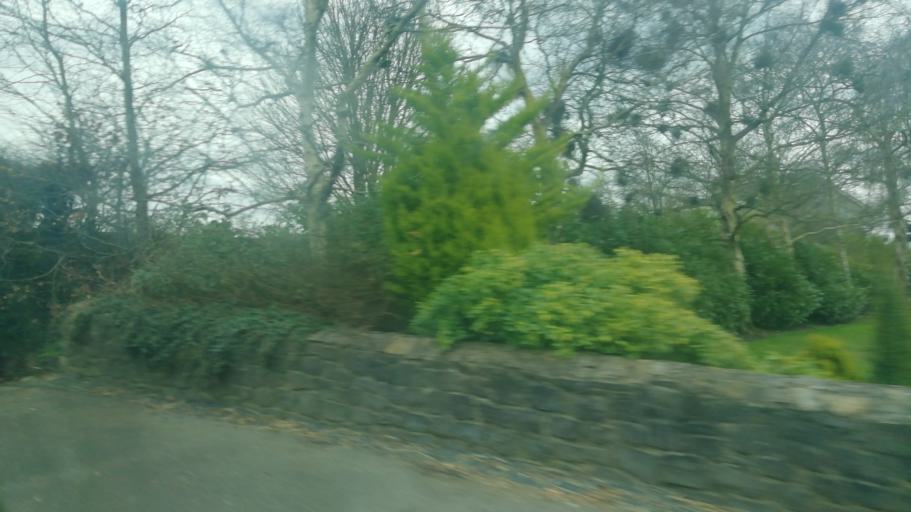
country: IE
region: Leinster
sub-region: Kildare
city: Maynooth
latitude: 53.3556
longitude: -6.6393
